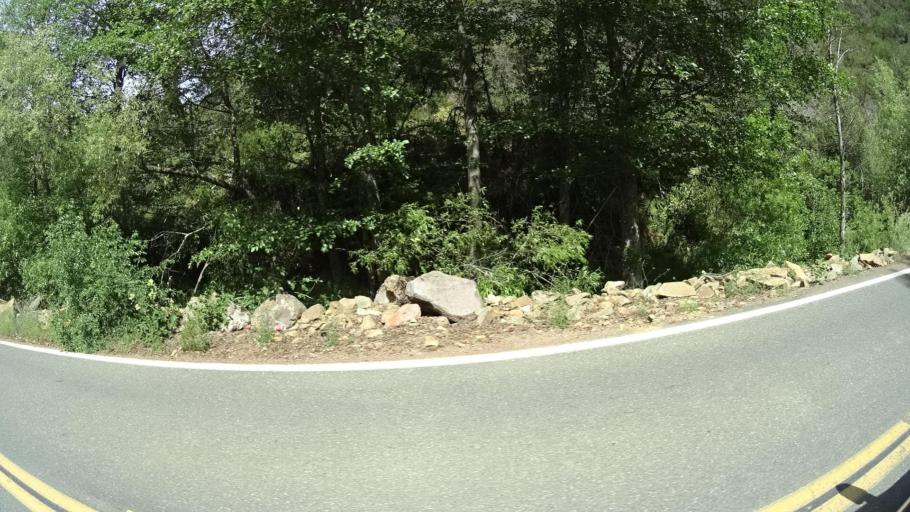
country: US
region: California
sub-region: Lake County
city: Lower Lake
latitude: 38.8942
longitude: -122.6587
